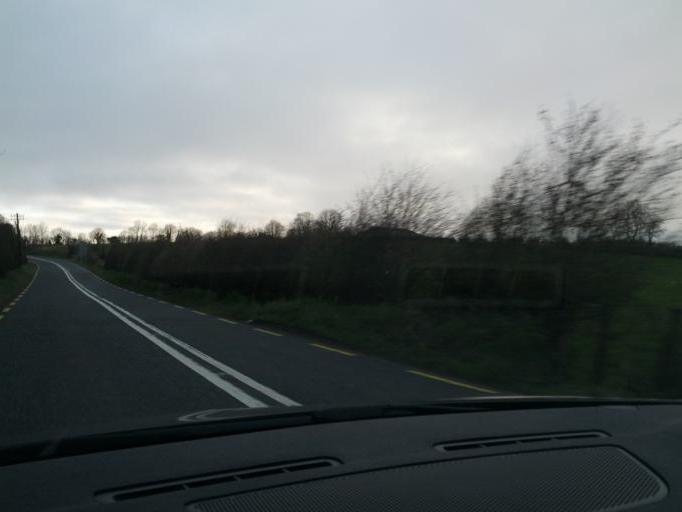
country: IE
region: Connaught
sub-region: Sligo
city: Ballymote
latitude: 54.1402
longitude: -8.5525
